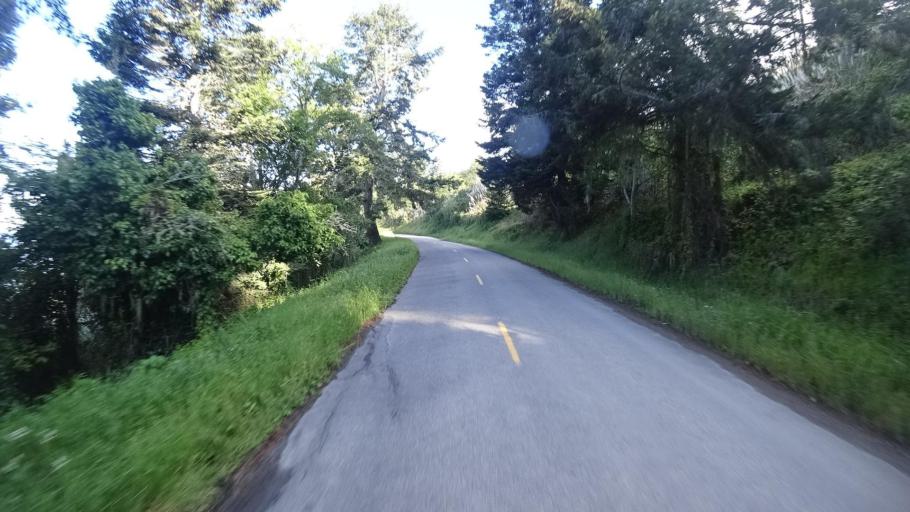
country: US
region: California
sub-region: Humboldt County
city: Westhaven-Moonstone
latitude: 41.0517
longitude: -124.1278
